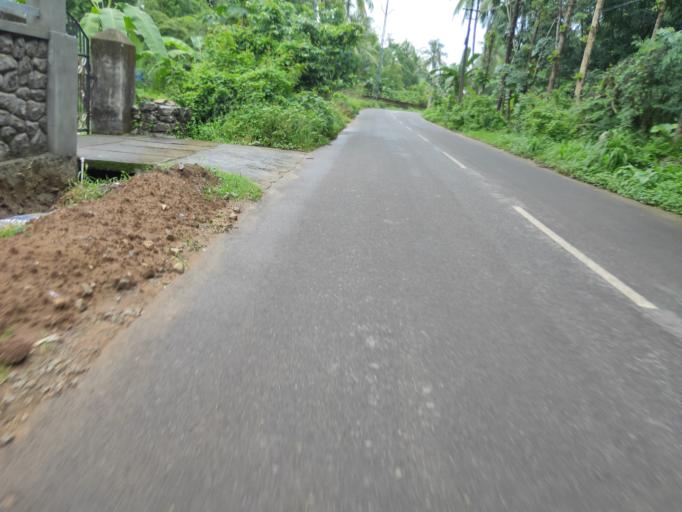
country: IN
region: Kerala
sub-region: Malappuram
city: Manjeri
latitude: 11.2270
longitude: 76.2732
